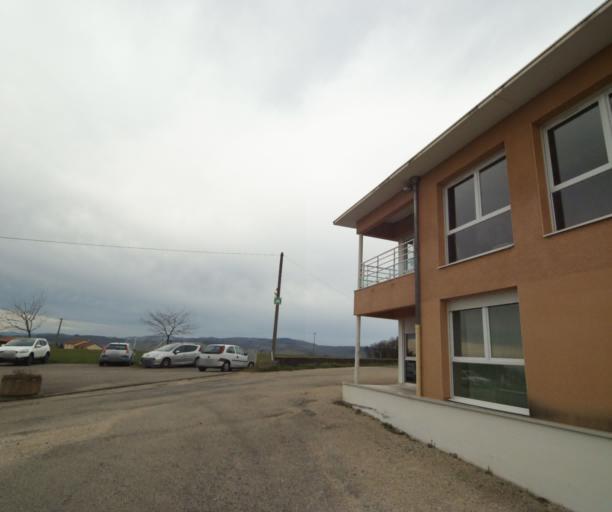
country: FR
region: Bourgogne
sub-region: Departement de Saone-et-Loire
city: Charnay-les-Macon
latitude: 46.3256
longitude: 4.7869
